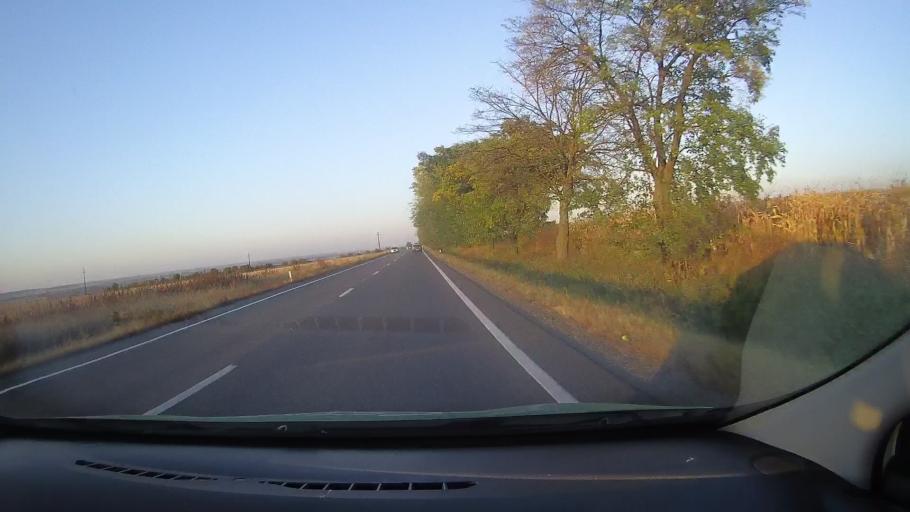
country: RO
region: Bihor
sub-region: Comuna Rosiori
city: Rosiori
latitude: 47.2709
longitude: 21.9757
